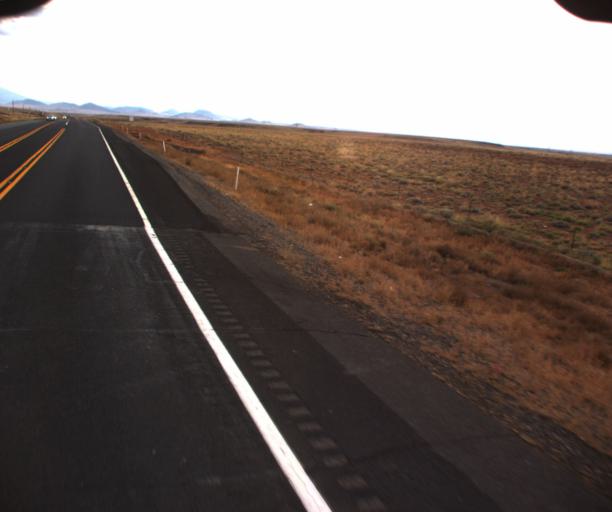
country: US
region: Arizona
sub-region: Coconino County
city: Tuba City
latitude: 35.7181
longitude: -111.4869
